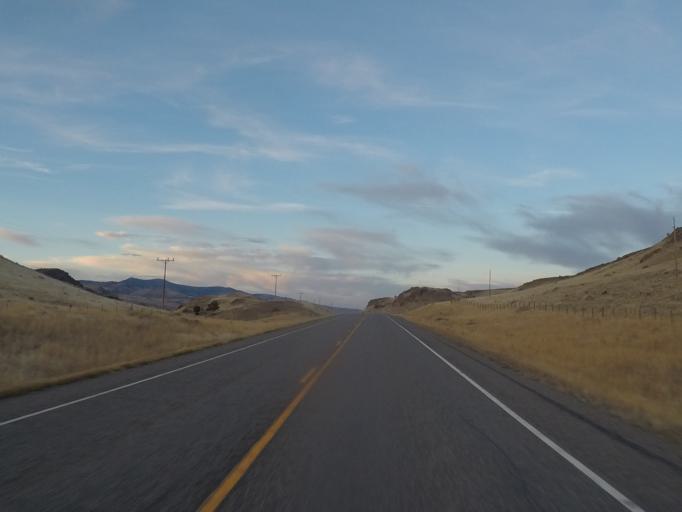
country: US
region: Montana
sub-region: Gallatin County
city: Bozeman
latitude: 45.2348
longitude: -110.8736
